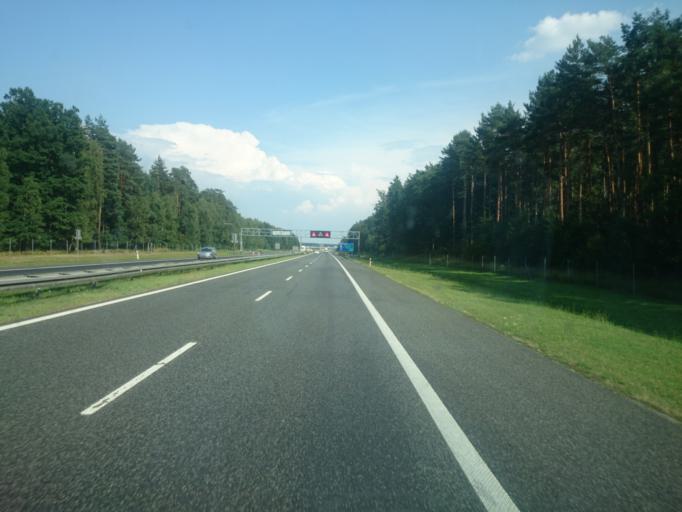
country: PL
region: Opole Voivodeship
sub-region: Powiat opolski
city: Niemodlin
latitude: 50.6659
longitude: 17.6821
